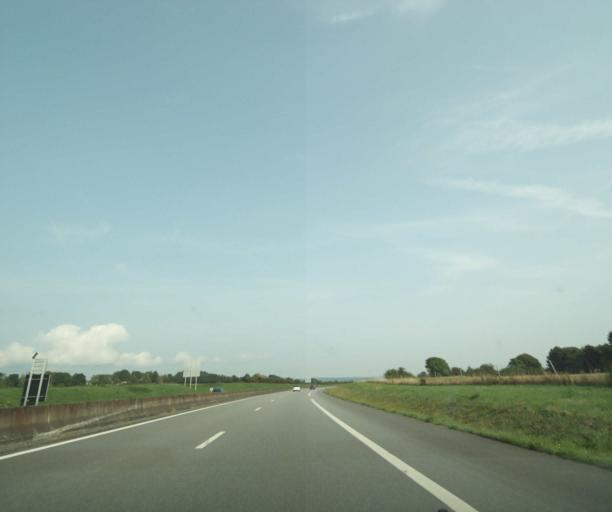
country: FR
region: Lower Normandy
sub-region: Departement de l'Orne
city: Valframbert
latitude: 48.4606
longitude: 0.1248
